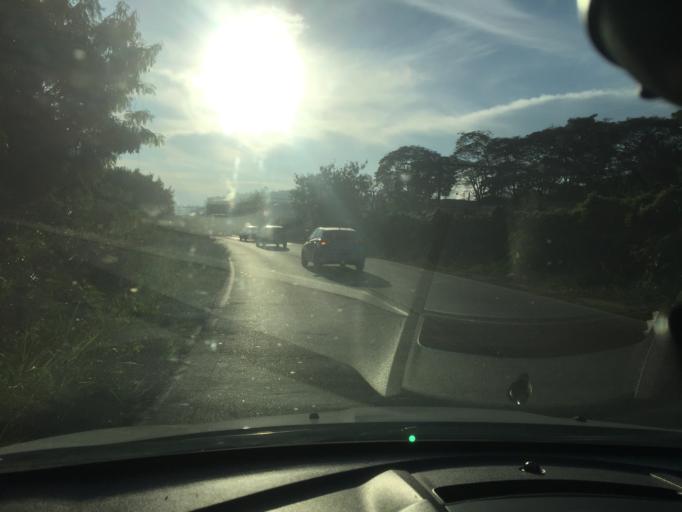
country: BR
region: Sao Paulo
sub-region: Varzea Paulista
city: Varzea Paulista
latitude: -23.2082
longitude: -46.8278
